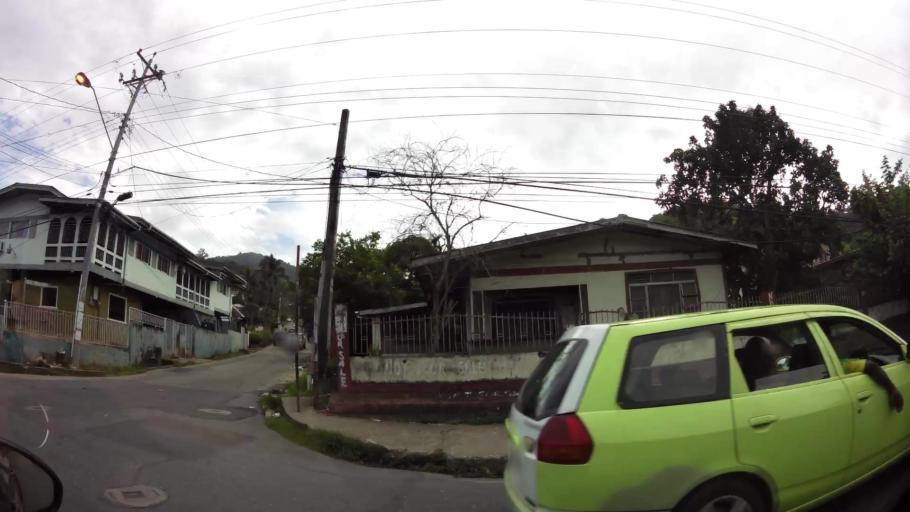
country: TT
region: San Juan/Laventille
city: Laventille
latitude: 10.6684
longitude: -61.4493
